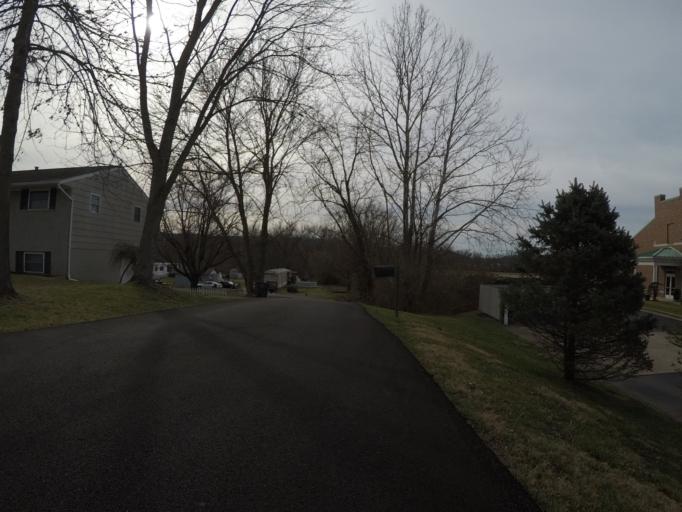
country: US
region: West Virginia
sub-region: Cabell County
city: Pea Ridge
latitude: 38.4454
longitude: -82.3735
